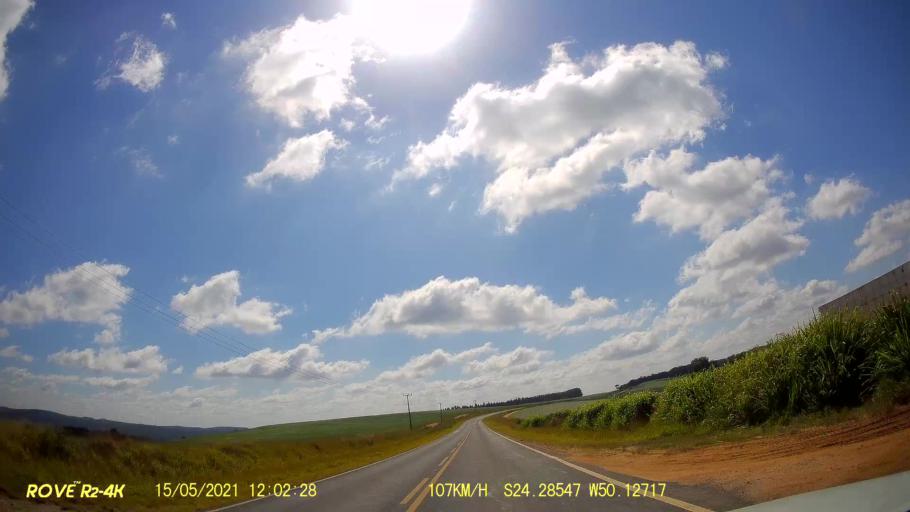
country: BR
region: Parana
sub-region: Pirai Do Sul
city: Pirai do Sul
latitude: -24.2854
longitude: -50.1272
